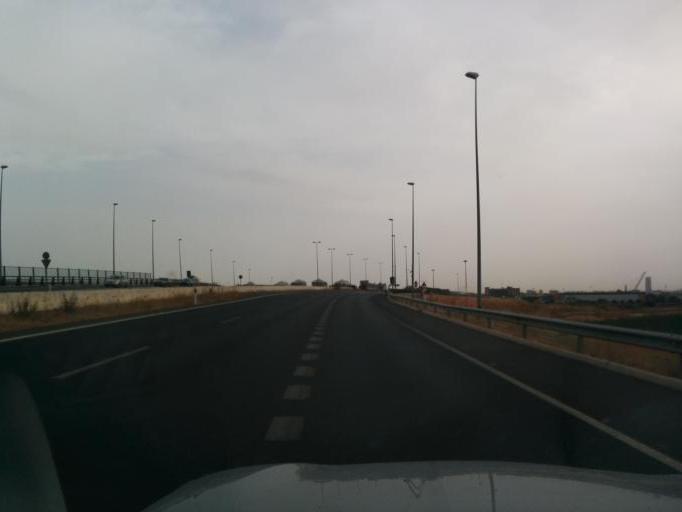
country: ES
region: Andalusia
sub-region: Provincia de Sevilla
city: La Algaba
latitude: 37.4398
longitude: -5.9719
